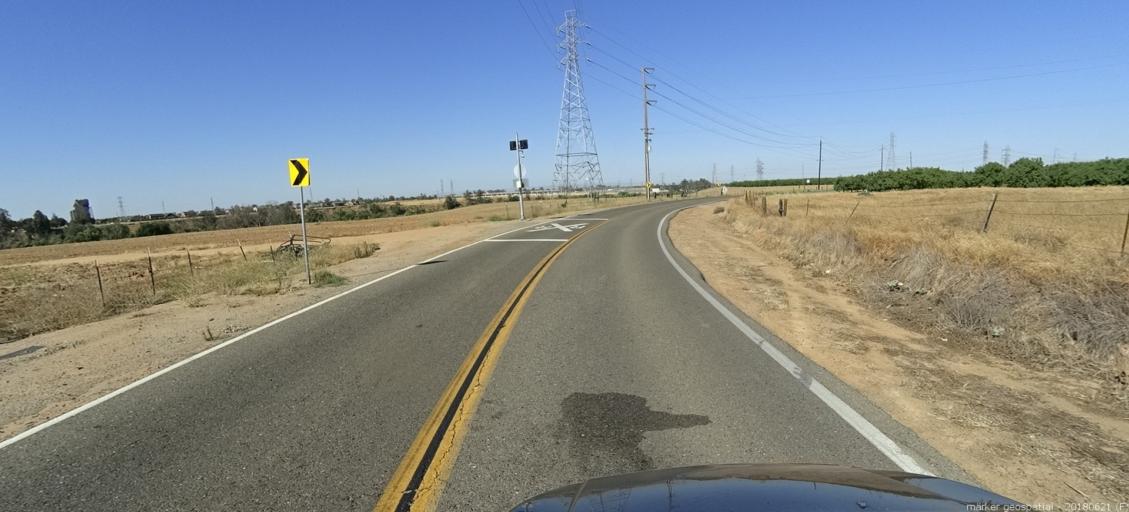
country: US
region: California
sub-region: Fresno County
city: Biola
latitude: 36.8520
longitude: -119.9100
